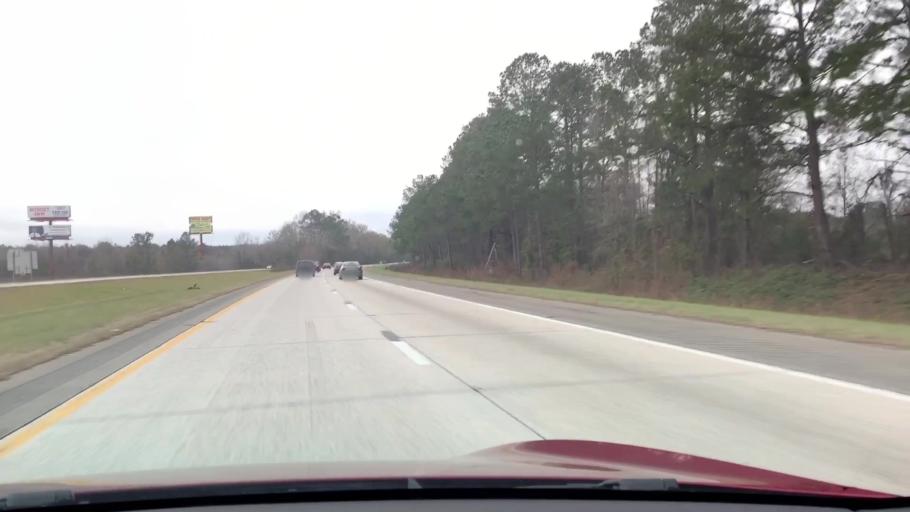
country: US
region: South Carolina
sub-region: Florence County
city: Timmonsville
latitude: 34.1396
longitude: -79.8800
